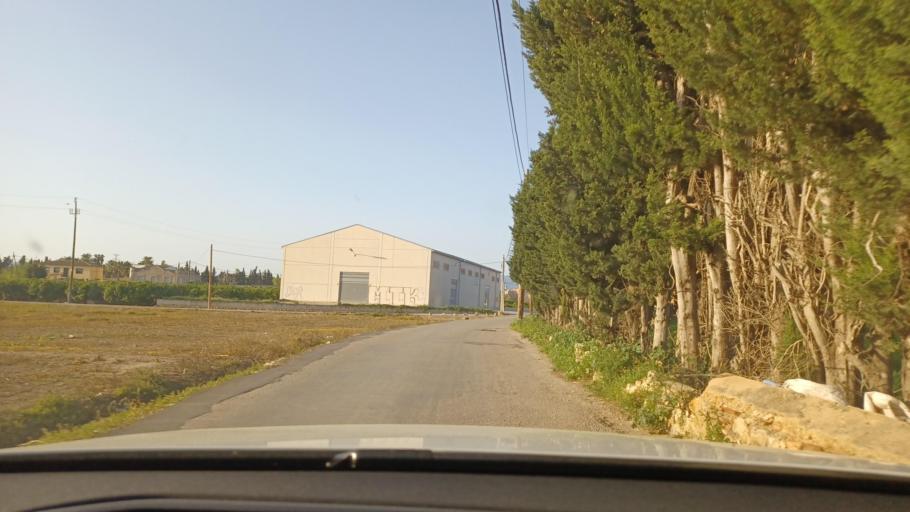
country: ES
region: Catalonia
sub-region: Provincia de Tarragona
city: Tortosa
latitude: 40.7978
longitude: 0.5170
